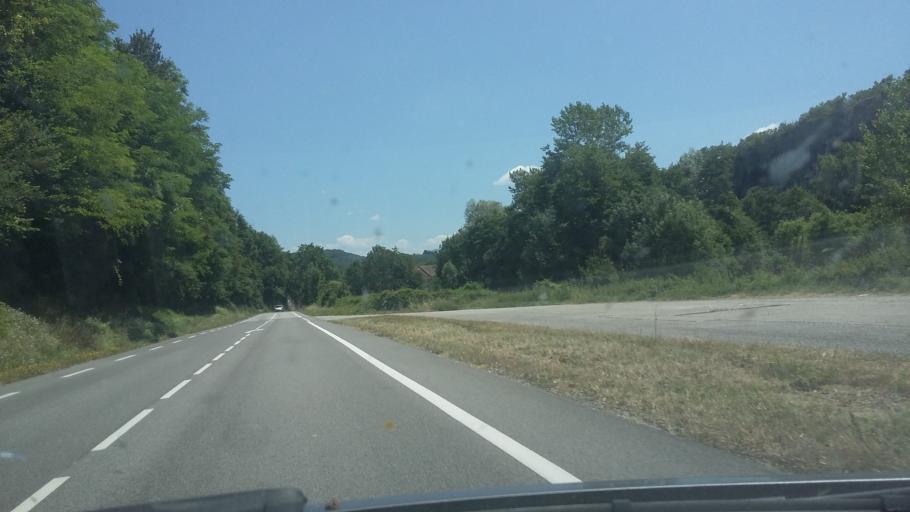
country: FR
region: Rhone-Alpes
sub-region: Departement de l'Ain
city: Virieu-le-Grand
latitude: 45.8129
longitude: 5.6635
